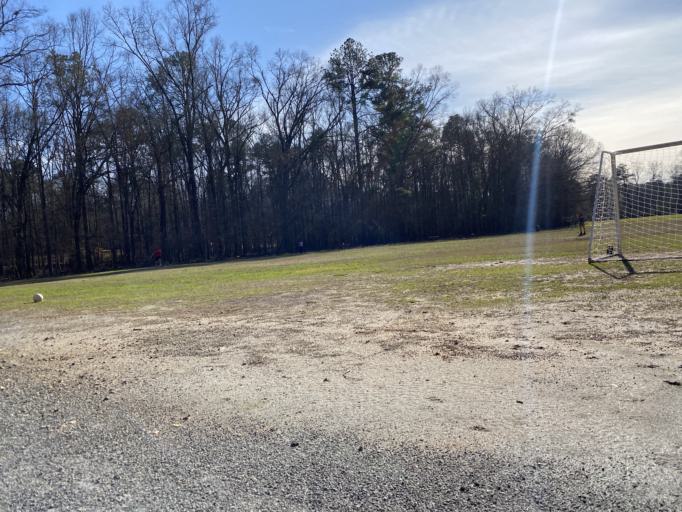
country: US
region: Georgia
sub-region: Cobb County
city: Kennesaw
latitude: 34.0530
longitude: -84.6346
